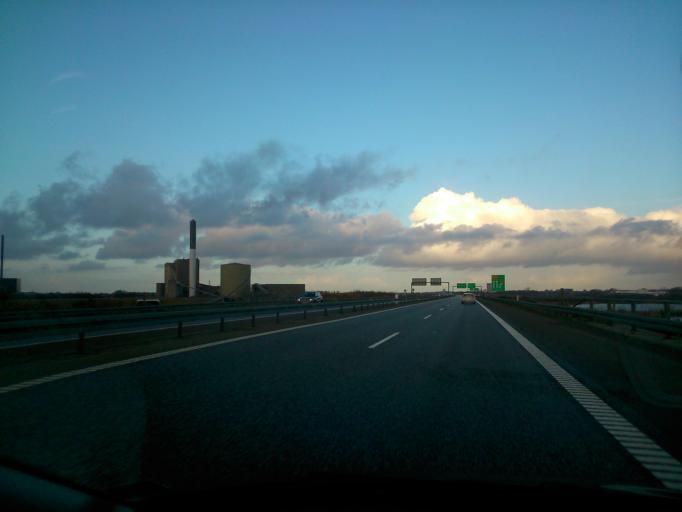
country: DK
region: Central Jutland
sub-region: Herning Kommune
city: Lind
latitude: 56.1157
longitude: 9.0111
